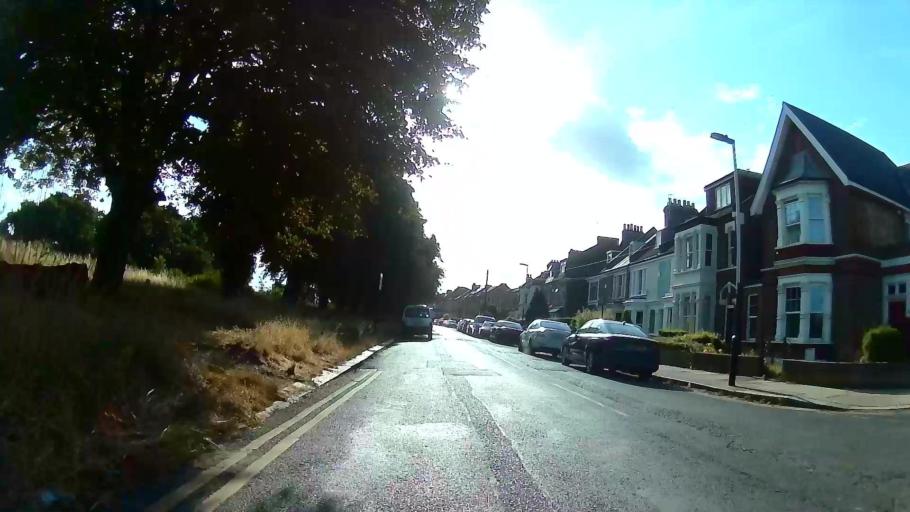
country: GB
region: England
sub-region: Greater London
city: East Ham
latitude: 51.5544
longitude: 0.0306
